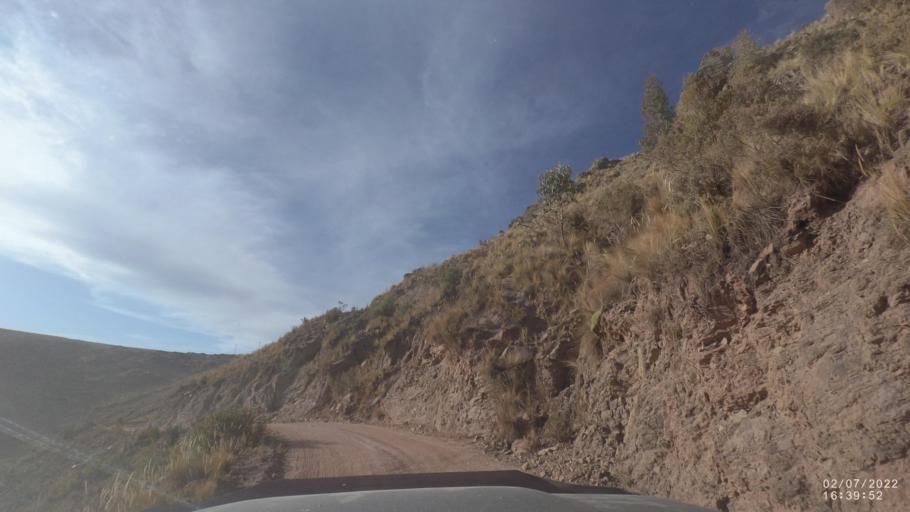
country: BO
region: Cochabamba
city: Irpa Irpa
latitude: -17.9747
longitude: -66.4953
